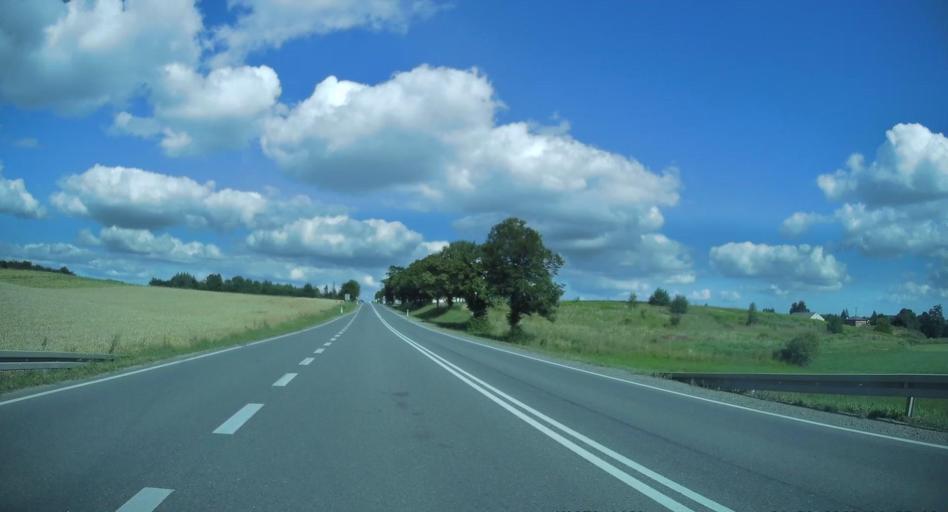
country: PL
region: Swietokrzyskie
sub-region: Powiat opatowski
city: Backowice
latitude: 50.7989
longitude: 21.2263
